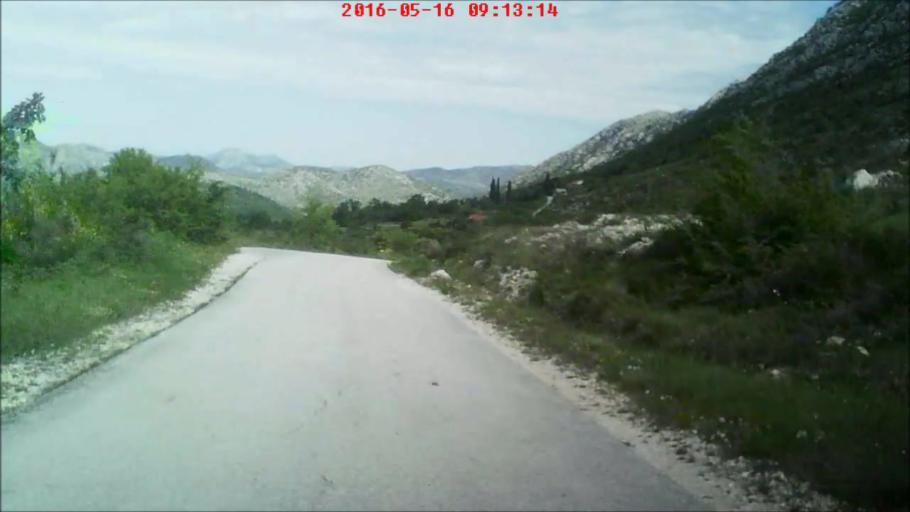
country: HR
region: Dubrovacko-Neretvanska
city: Podgora
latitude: 42.8312
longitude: 17.8467
